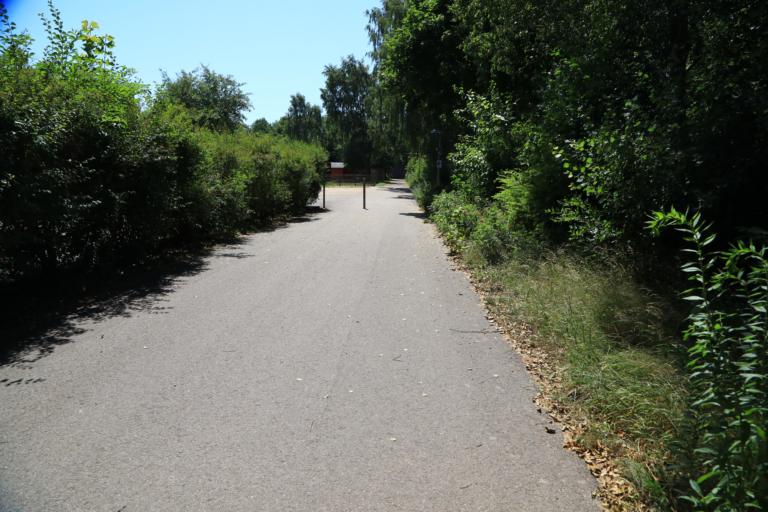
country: SE
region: Halland
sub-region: Halmstads Kommun
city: Fyllinge
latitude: 56.6660
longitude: 12.9099
